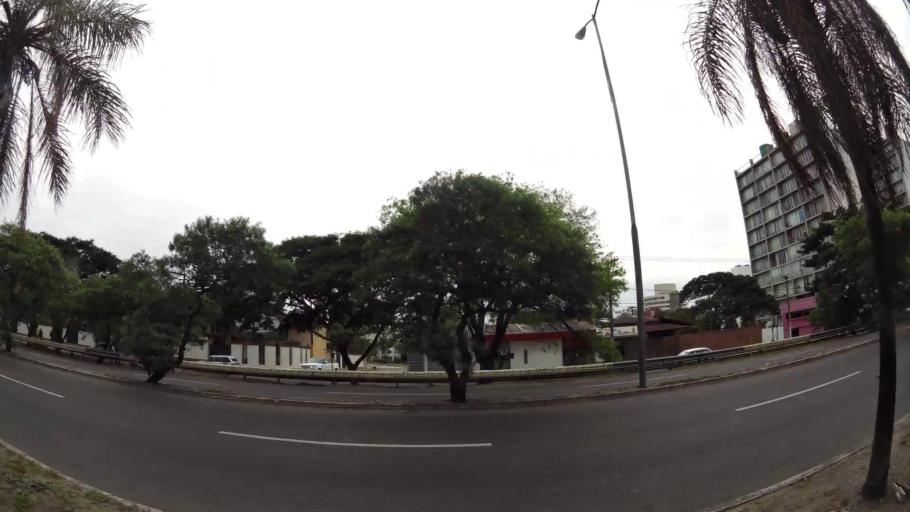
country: BO
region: Santa Cruz
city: Santa Cruz de la Sierra
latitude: -17.7945
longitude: -63.1940
